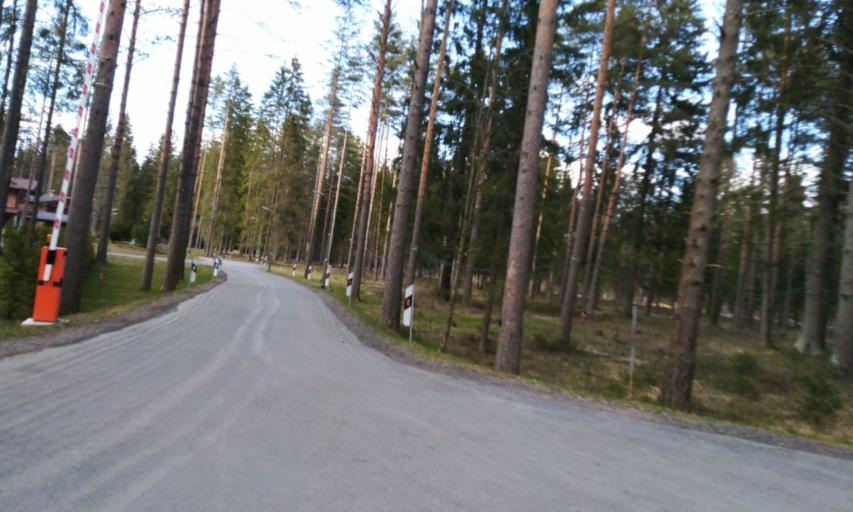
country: RU
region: Leningrad
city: Toksovo
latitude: 60.1274
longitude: 30.4600
